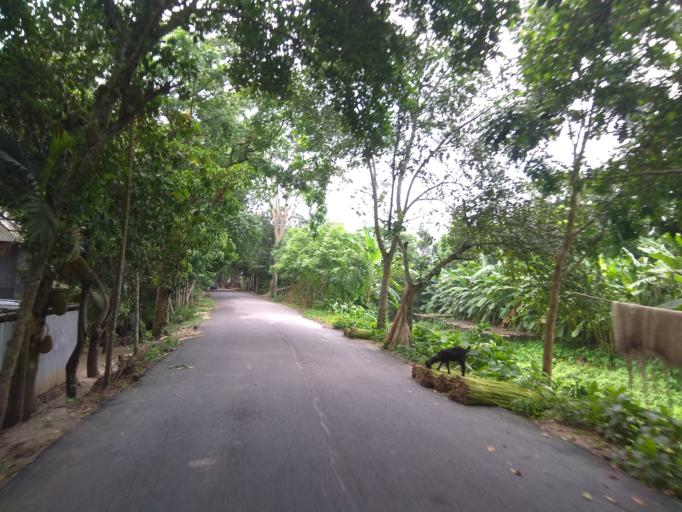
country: BD
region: Dhaka
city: Dohar
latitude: 23.4434
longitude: 90.0647
